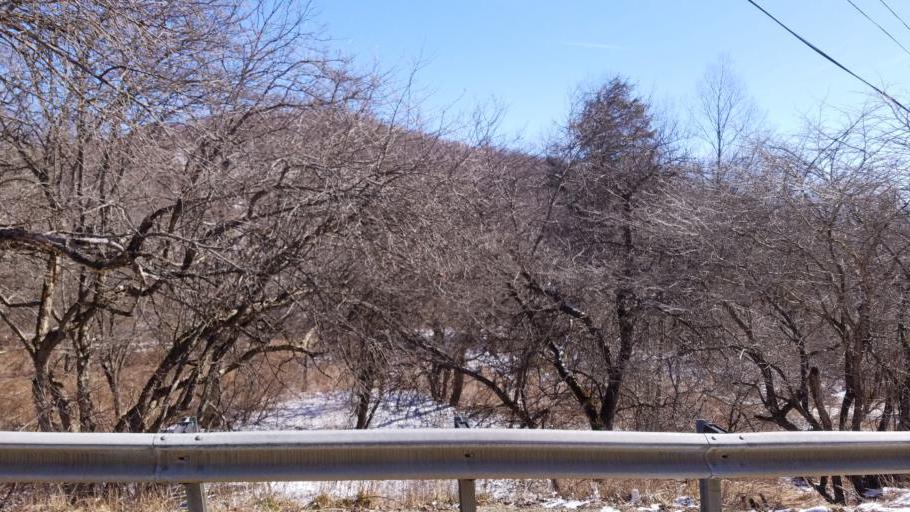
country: US
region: New York
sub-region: Allegany County
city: Andover
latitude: 41.9348
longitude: -77.8033
